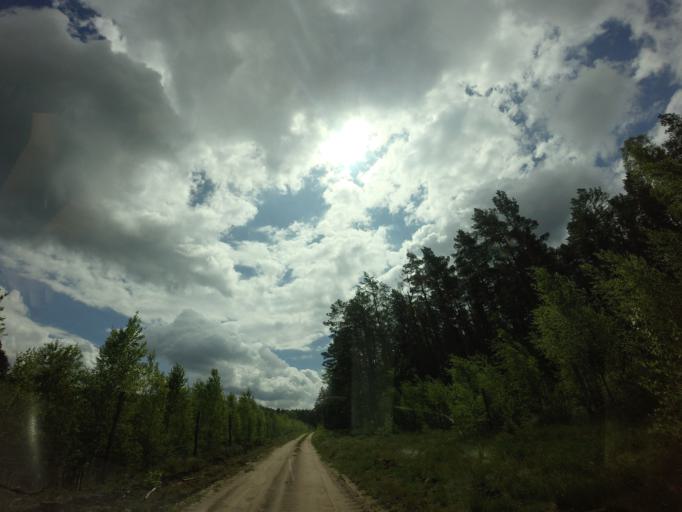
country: PL
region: West Pomeranian Voivodeship
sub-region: Powiat drawski
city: Kalisz Pomorski
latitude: 53.1677
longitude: 15.8961
